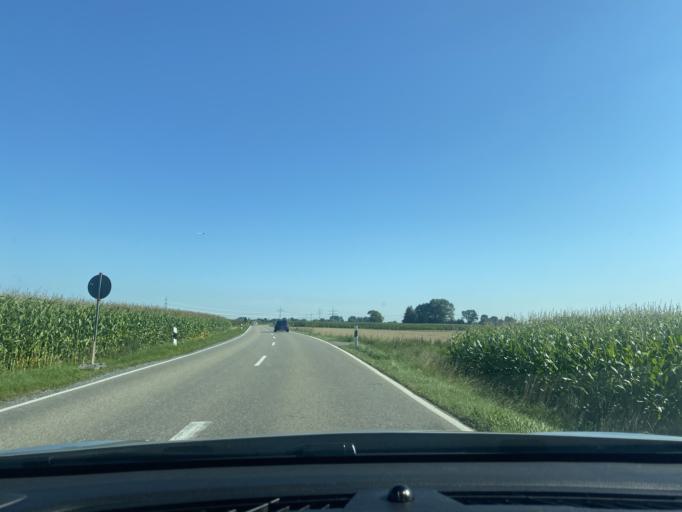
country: DE
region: Bavaria
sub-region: Upper Bavaria
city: Erding
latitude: 48.3315
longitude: 11.8942
